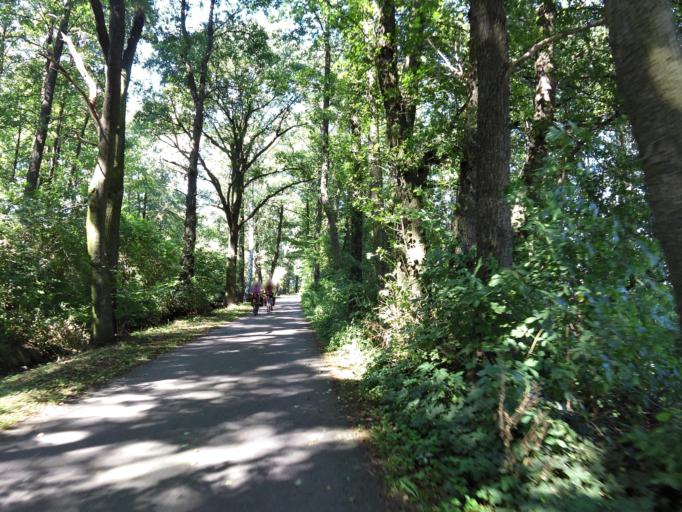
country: DE
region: Saxony
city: Torgau
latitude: 51.5143
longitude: 13.0238
